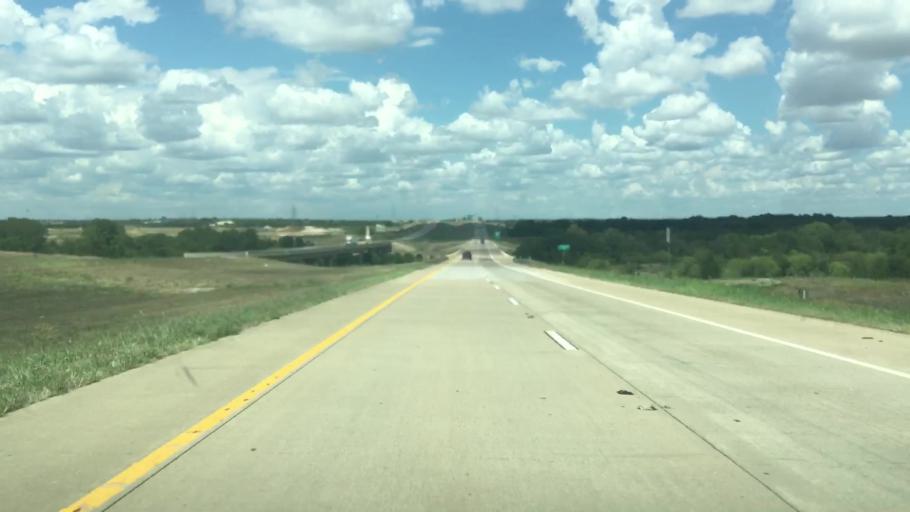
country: US
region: Texas
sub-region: Williamson County
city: Georgetown
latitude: 30.6519
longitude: -97.6349
